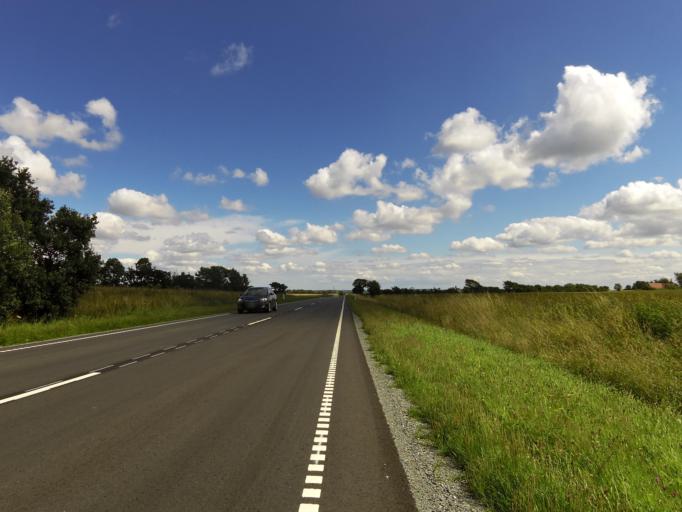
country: DK
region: South Denmark
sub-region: Haderslev Kommune
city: Gram
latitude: 55.3133
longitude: 9.1192
